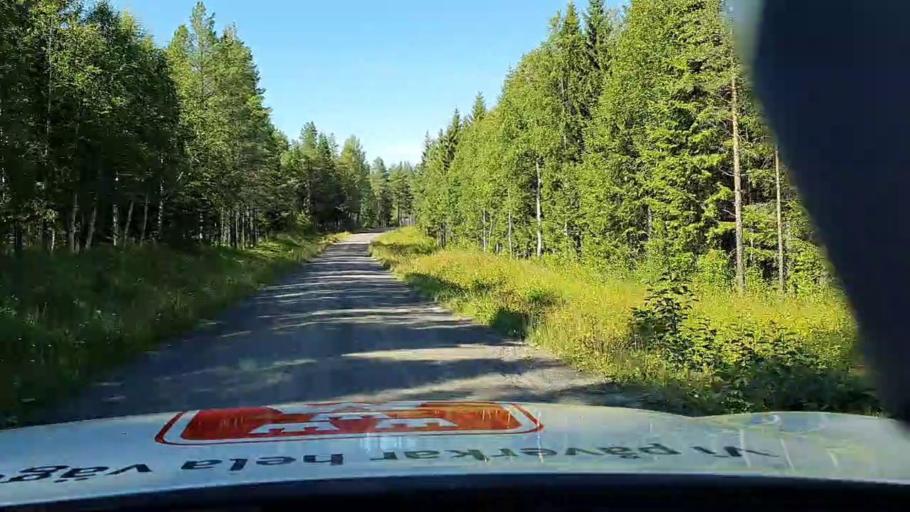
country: SE
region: Jaemtland
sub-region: OEstersunds Kommun
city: Lit
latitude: 63.7675
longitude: 14.6582
